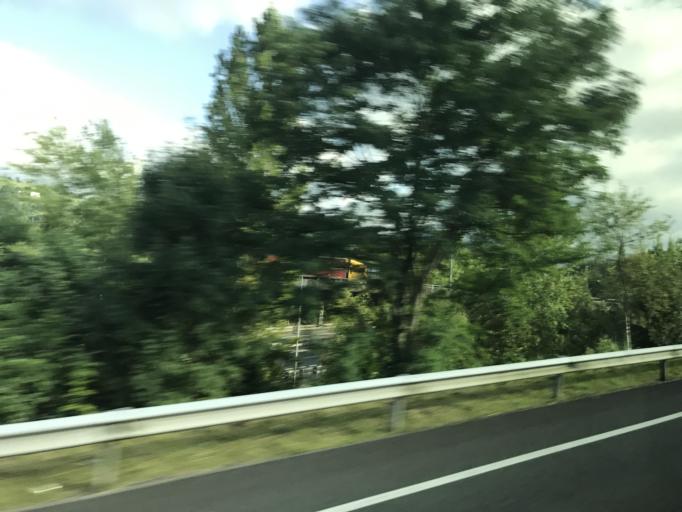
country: ES
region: Basque Country
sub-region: Provincia de Guipuzcoa
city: Astigarraga
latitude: 43.2853
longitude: -1.9583
